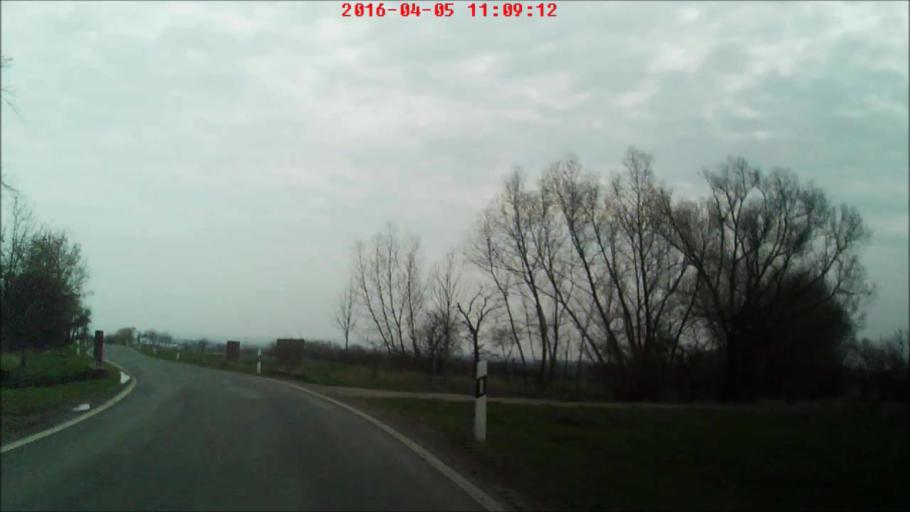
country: DE
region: Thuringia
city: Bienstadt
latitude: 51.0156
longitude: 10.8517
